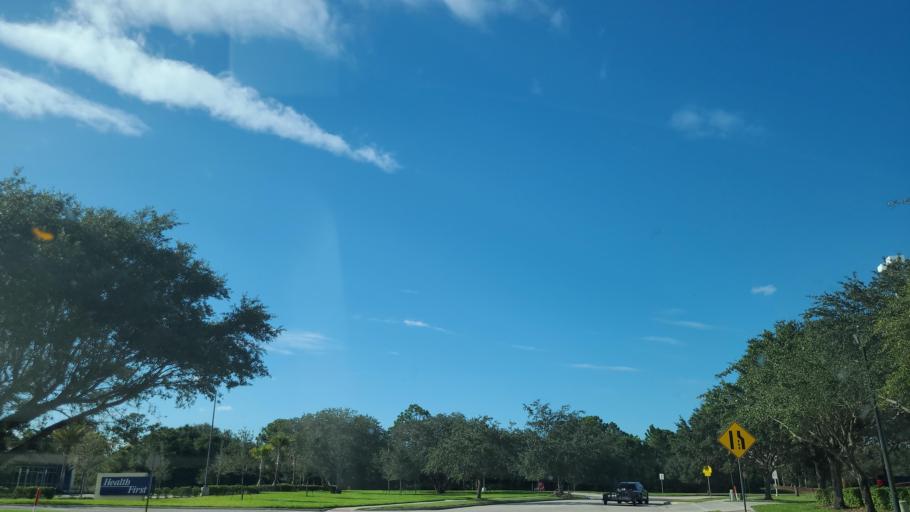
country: US
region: Florida
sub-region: Brevard County
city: Grant-Valkaria
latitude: 27.9504
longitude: -80.6590
